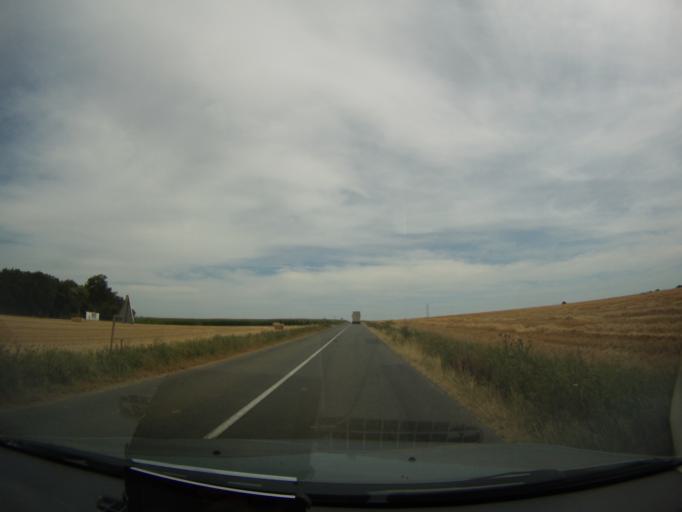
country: FR
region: Poitou-Charentes
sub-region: Departement de la Vienne
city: Mirebeau
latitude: 46.7318
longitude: 0.1935
